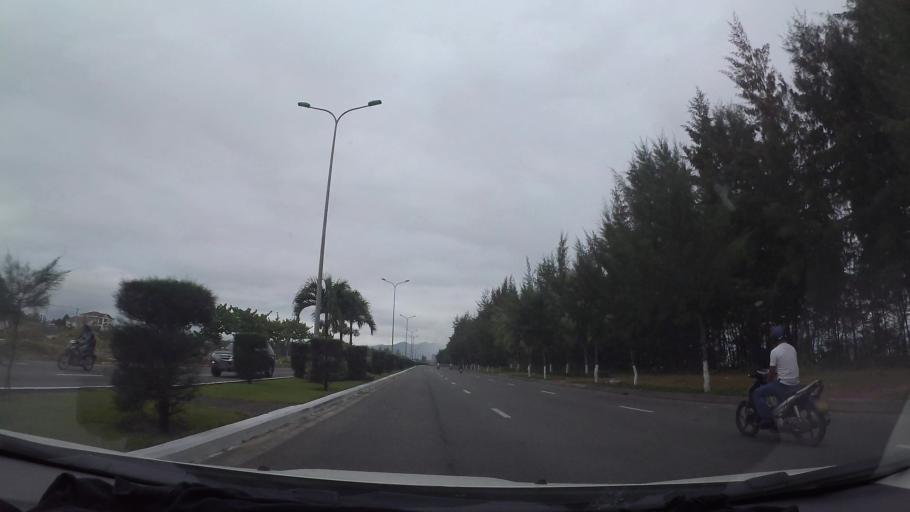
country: VN
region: Da Nang
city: Lien Chieu
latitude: 16.0927
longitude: 108.1490
